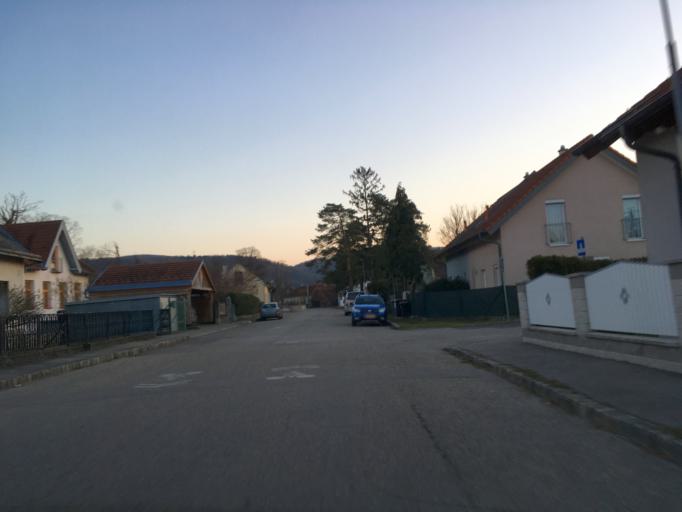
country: AT
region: Lower Austria
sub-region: Politischer Bezirk Tulln
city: Wordern
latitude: 48.3318
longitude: 16.2086
